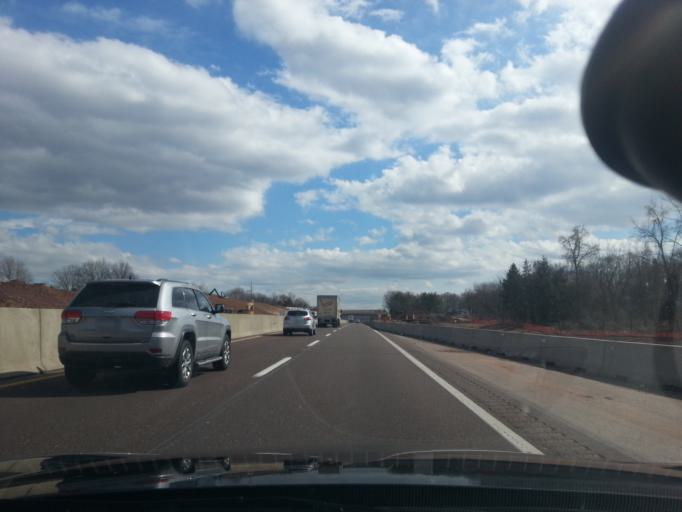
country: US
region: Pennsylvania
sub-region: Montgomery County
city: Kulpsville
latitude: 40.2143
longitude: -75.3263
